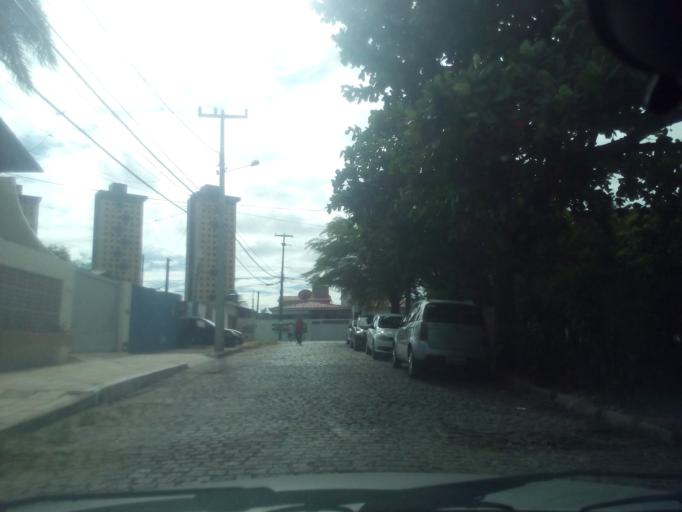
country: BR
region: Rio Grande do Norte
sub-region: Parnamirim
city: Parnamirim
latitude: -5.8703
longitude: -35.2092
